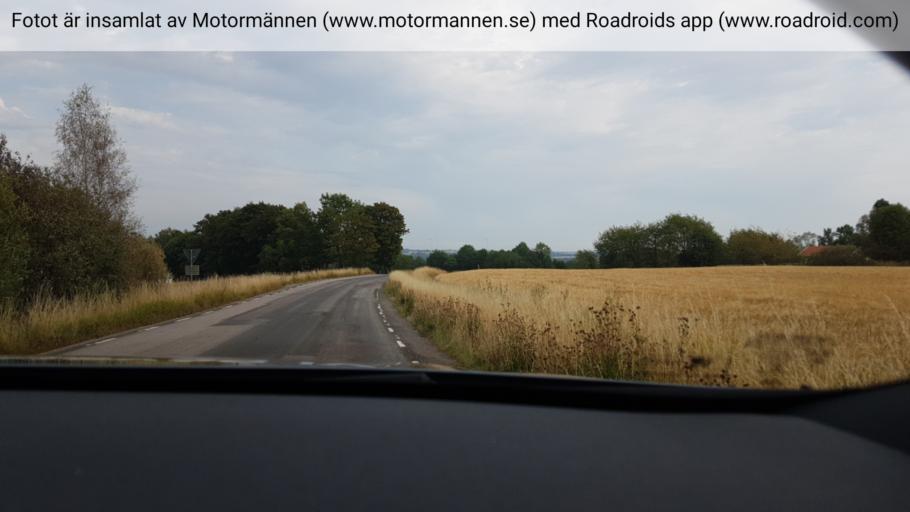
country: SE
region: Vaestra Goetaland
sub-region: Falkopings Kommun
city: Akarp
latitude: 58.1779
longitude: 13.6370
